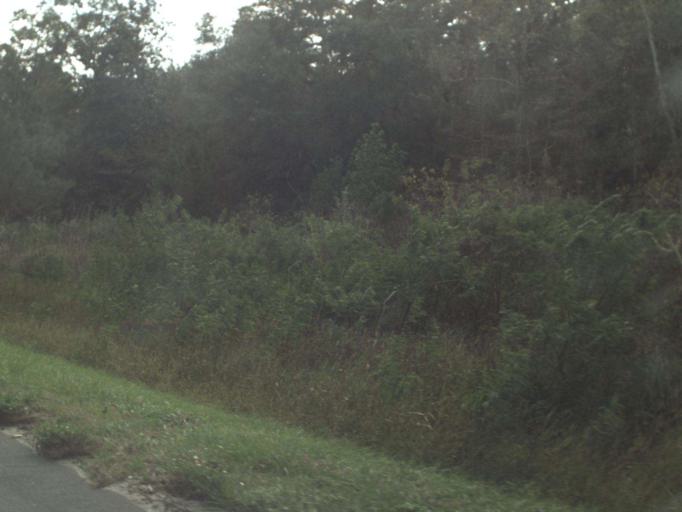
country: US
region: Florida
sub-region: Franklin County
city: Carrabelle
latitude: 29.9933
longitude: -84.5034
